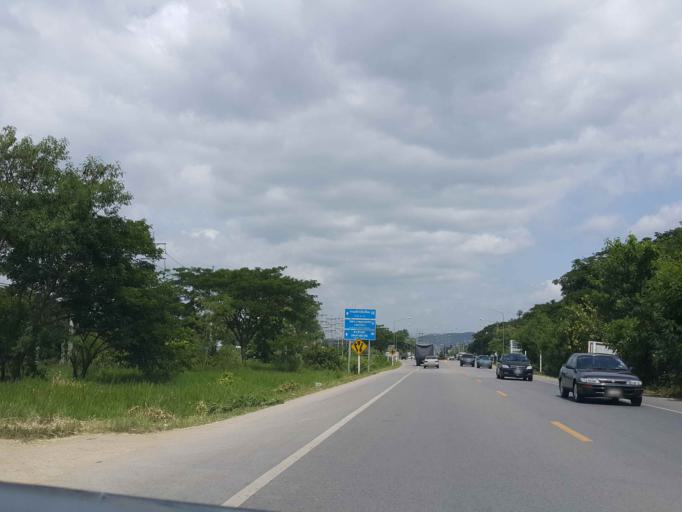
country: TH
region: Chiang Mai
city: Hang Dong
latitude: 18.7224
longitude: 98.9496
